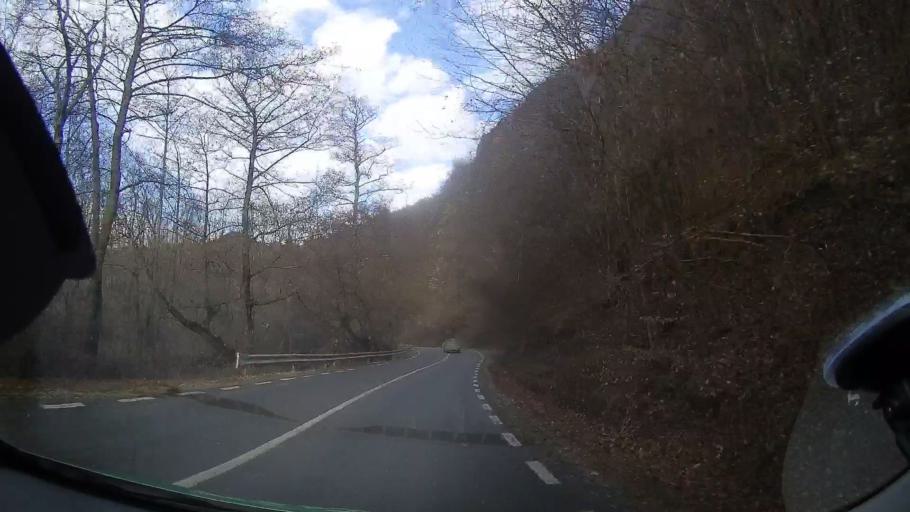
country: RO
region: Cluj
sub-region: Comuna Baisoara
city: Baisoara
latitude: 46.6034
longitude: 23.4246
